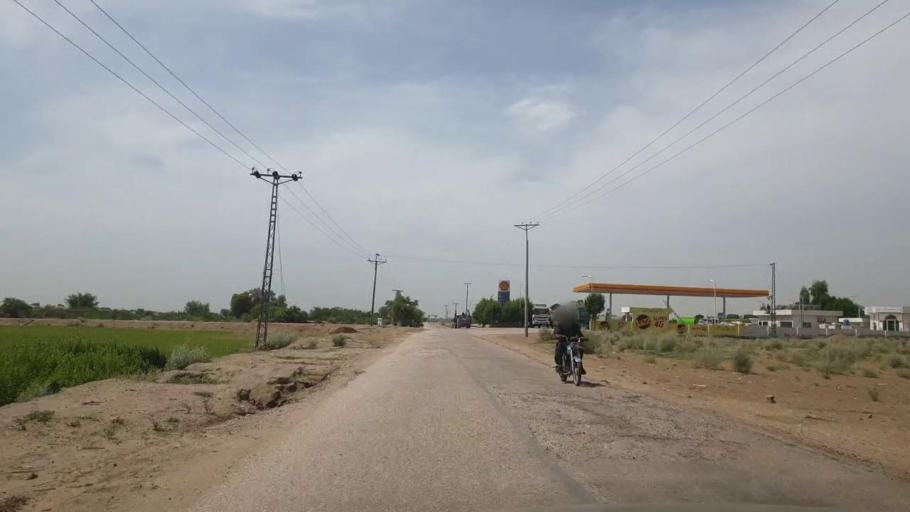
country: PK
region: Sindh
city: Kot Diji
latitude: 27.1474
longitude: 68.9625
